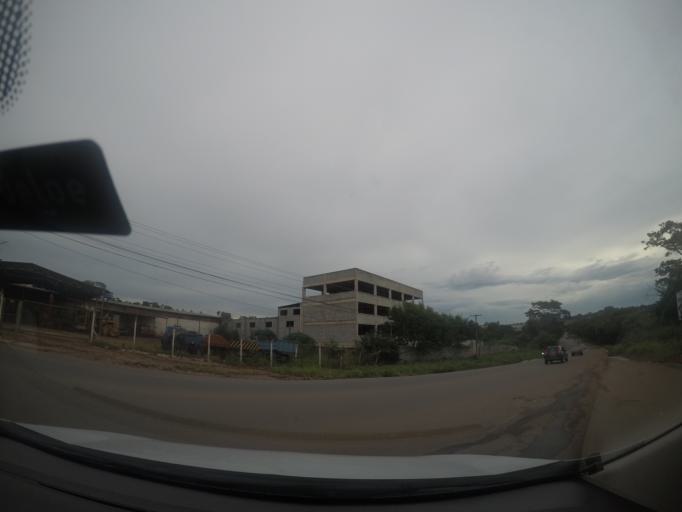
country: BR
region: Goias
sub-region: Goiania
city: Goiania
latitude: -16.6294
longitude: -49.2384
